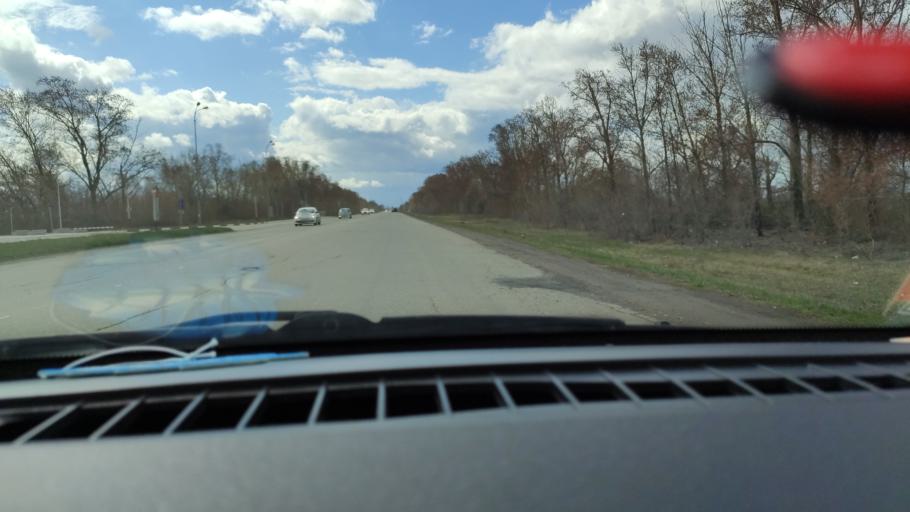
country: RU
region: Samara
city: Tol'yatti
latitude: 53.5911
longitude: 49.4064
